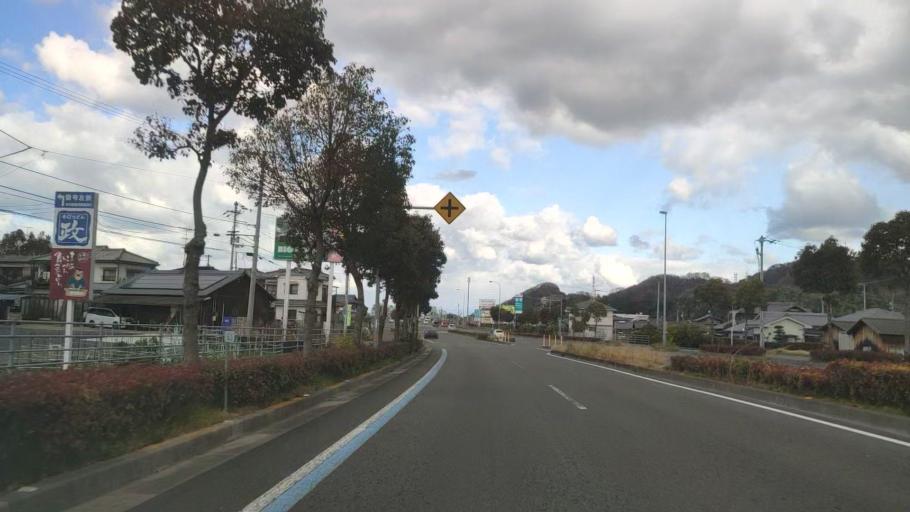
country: JP
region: Ehime
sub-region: Shikoku-chuo Shi
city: Matsuyama
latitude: 33.8972
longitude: 132.7581
